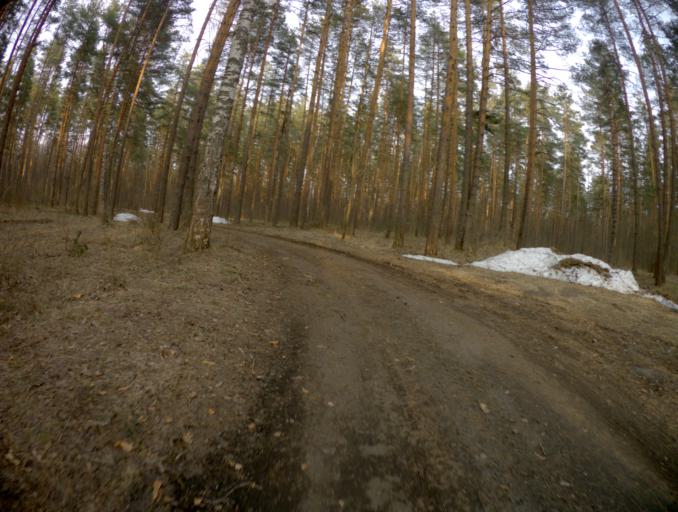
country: RU
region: Vladimir
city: Kommunar
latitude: 56.0717
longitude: 40.4403
